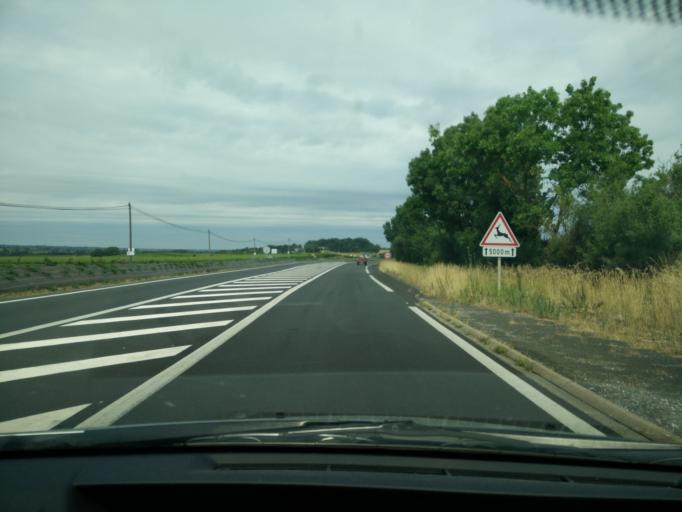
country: FR
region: Pays de la Loire
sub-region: Departement de Maine-et-Loire
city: Brissac-Quince
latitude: 47.3655
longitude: -0.4537
